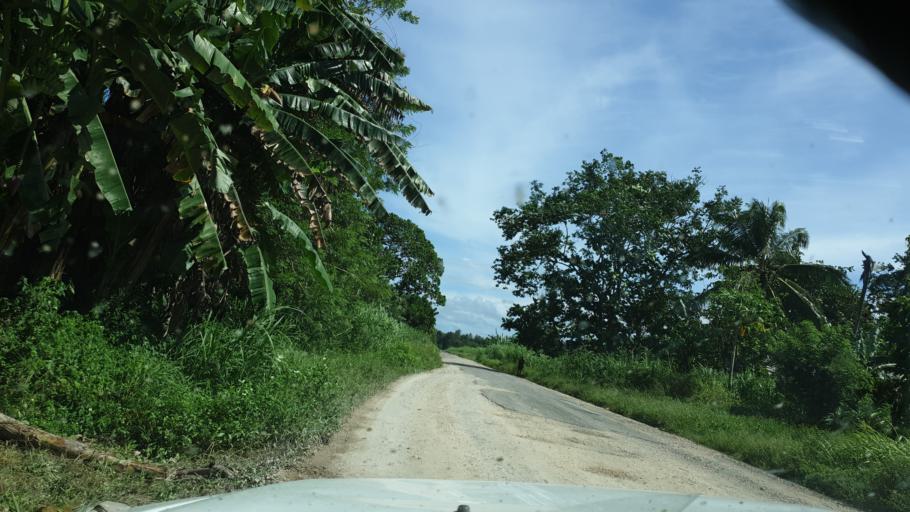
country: PG
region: Madang
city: Madang
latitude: -4.7231
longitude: 145.6404
